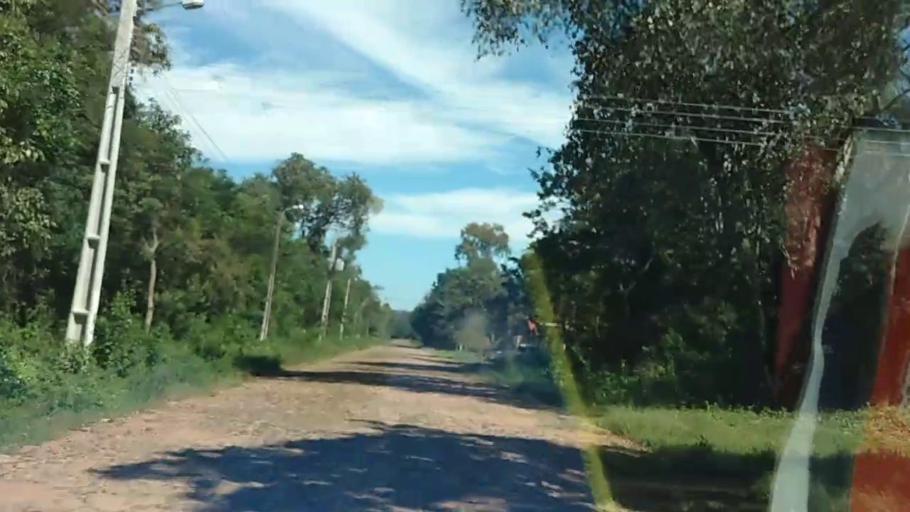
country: PY
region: Cordillera
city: San Bernardino
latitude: -25.3306
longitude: -57.2696
